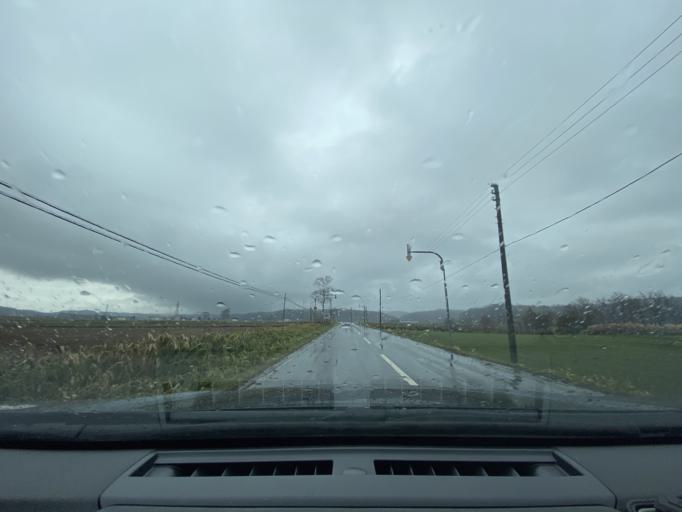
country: JP
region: Hokkaido
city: Fukagawa
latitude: 43.8293
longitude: 141.8973
